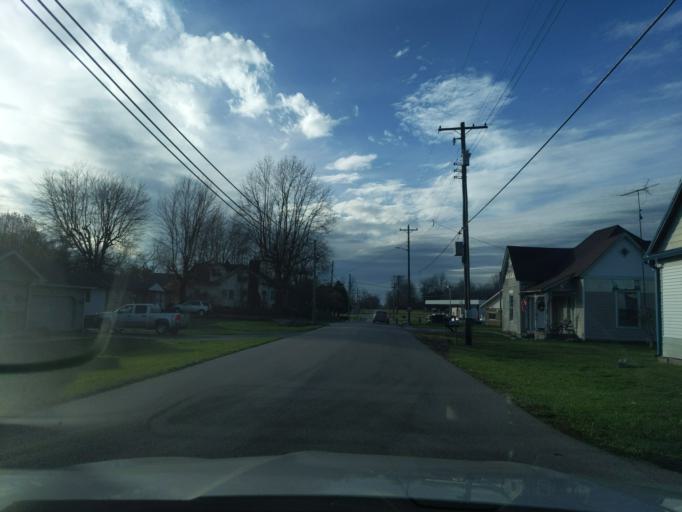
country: US
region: Indiana
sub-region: Decatur County
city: Westport
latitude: 39.1758
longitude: -85.5802
